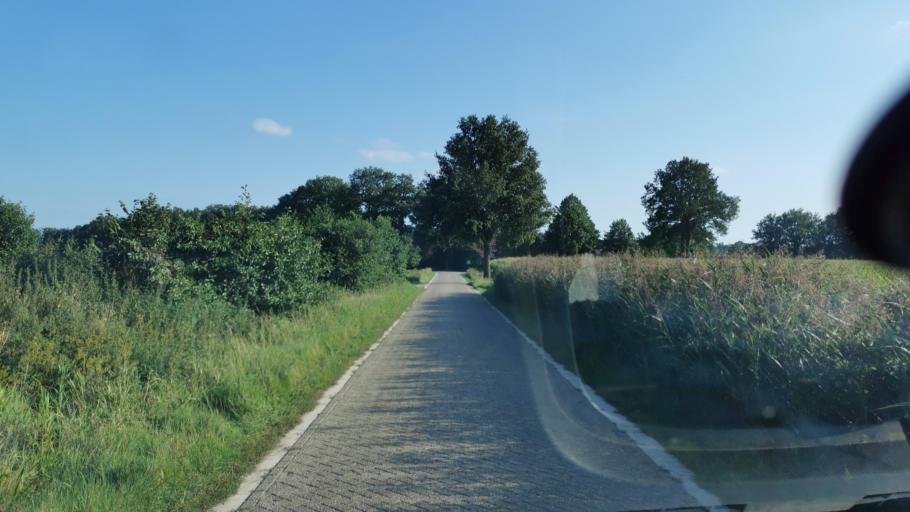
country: NL
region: Overijssel
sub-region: Gemeente Tubbergen
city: Tubbergen
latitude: 52.3491
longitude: 6.8359
